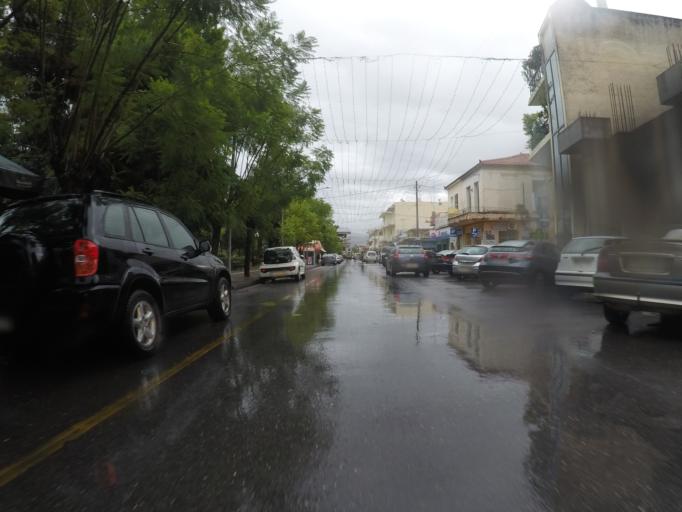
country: GR
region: Peloponnese
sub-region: Nomos Messinias
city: Messini
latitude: 37.0509
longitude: 22.0079
